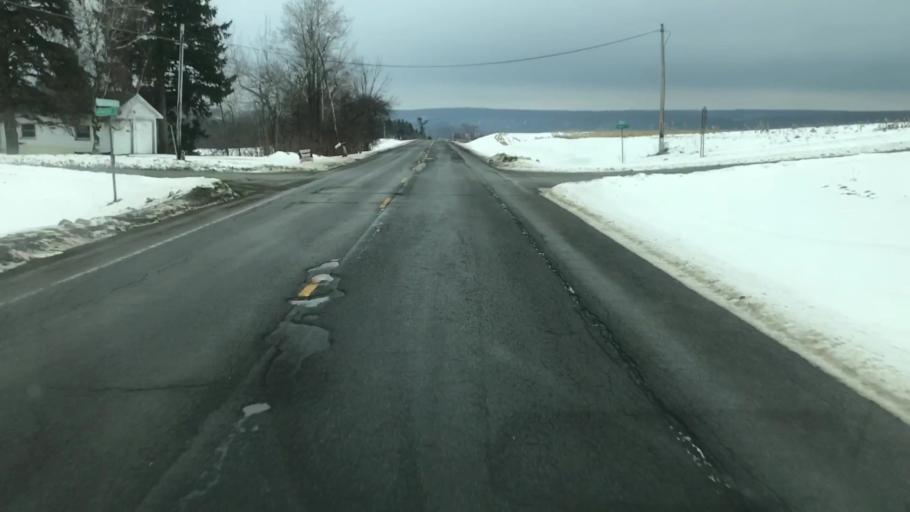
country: US
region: New York
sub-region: Cayuga County
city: Moravia
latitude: 42.7154
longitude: -76.3128
